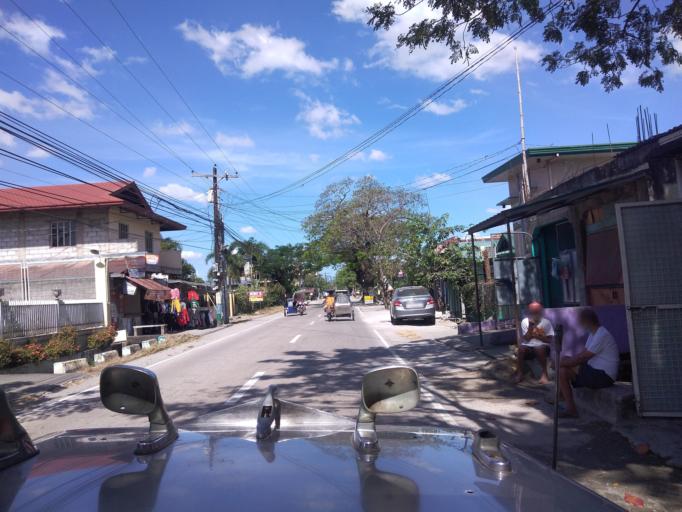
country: PH
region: Central Luzon
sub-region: Province of Pampanga
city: Santa Rita
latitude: 15.0006
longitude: 120.6106
